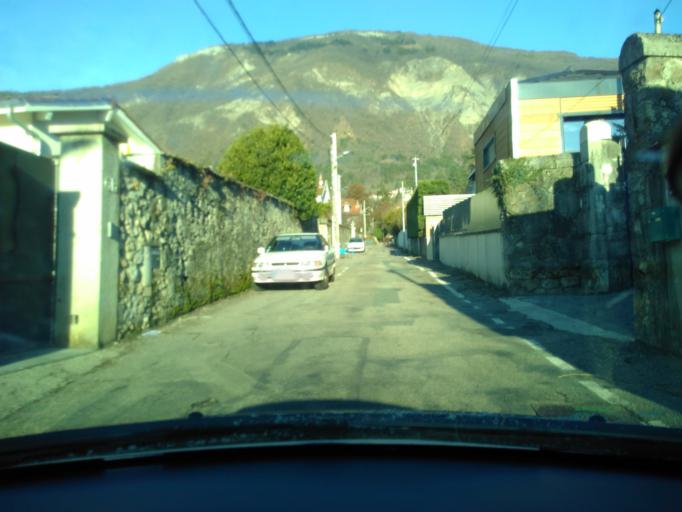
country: FR
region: Rhone-Alpes
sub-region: Departement de l'Isere
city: La Tronche
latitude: 45.2078
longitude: 5.7504
